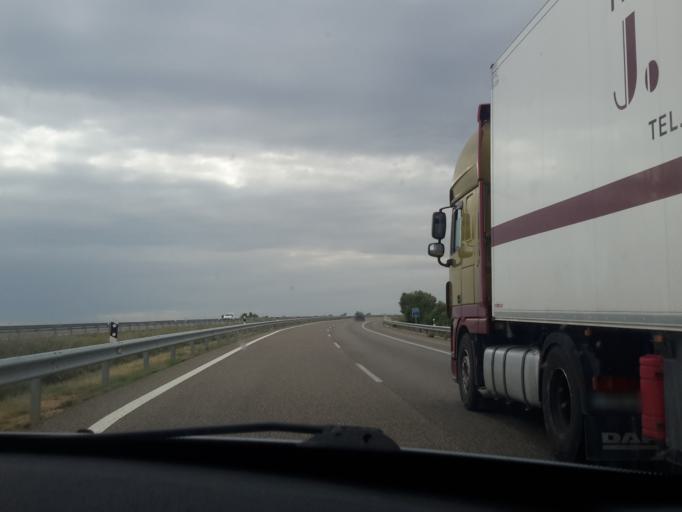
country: ES
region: Aragon
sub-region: Provincia de Huesca
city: Candasnos
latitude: 41.4962
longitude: 0.1219
